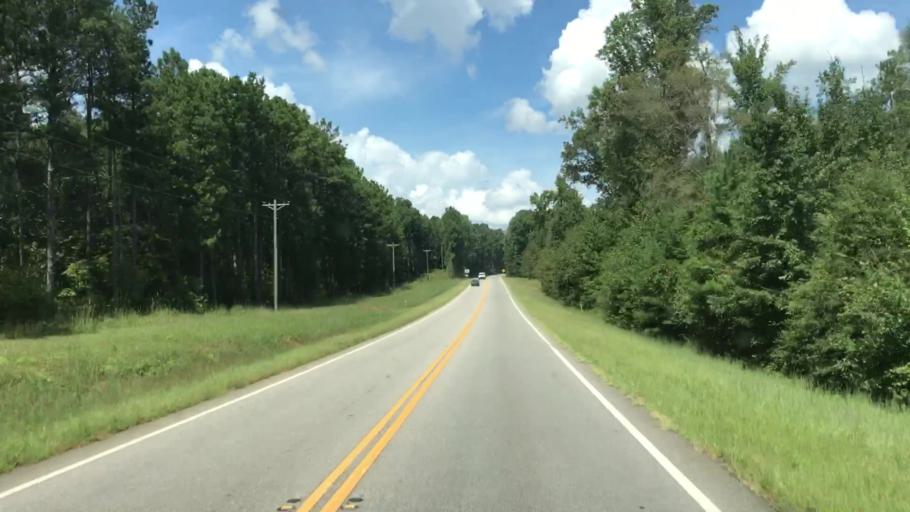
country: US
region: Georgia
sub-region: Greene County
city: Greensboro
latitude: 33.6763
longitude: -83.2680
